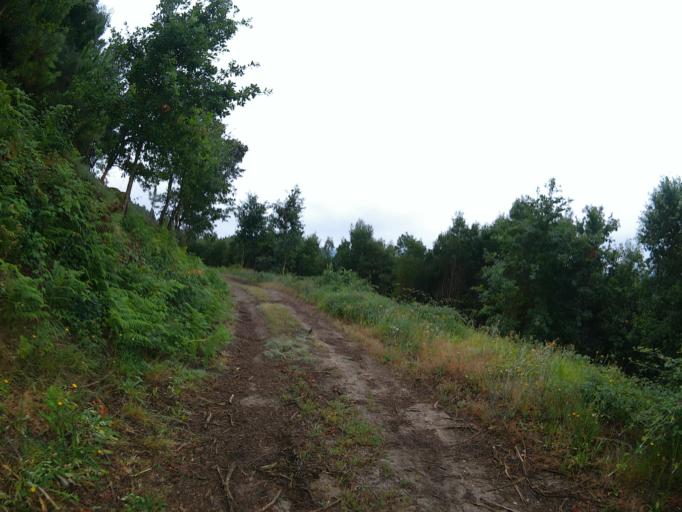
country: PT
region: Viana do Castelo
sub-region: Ponte de Lima
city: Ponte de Lima
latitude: 41.7217
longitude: -8.6094
